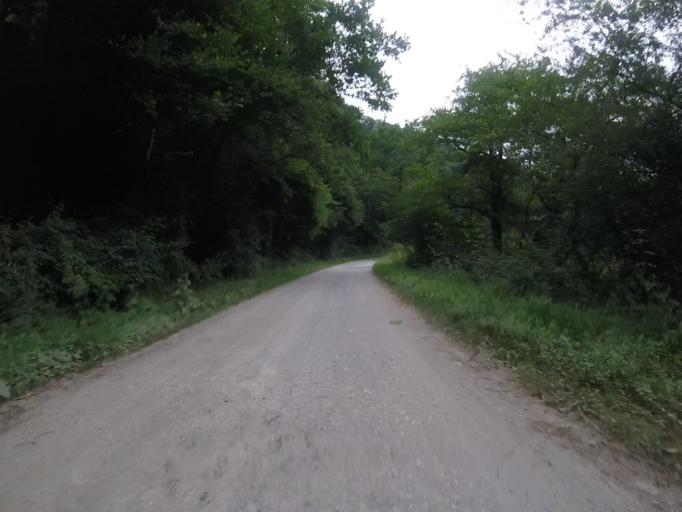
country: ES
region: Navarre
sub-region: Provincia de Navarra
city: Sunbilla
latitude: 43.1888
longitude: -1.6757
